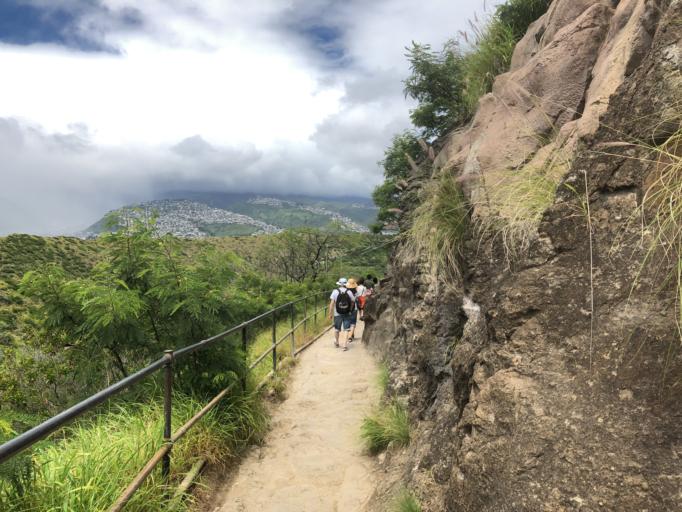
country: US
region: Hawaii
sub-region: Honolulu County
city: Honolulu
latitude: 21.2611
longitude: -157.8106
